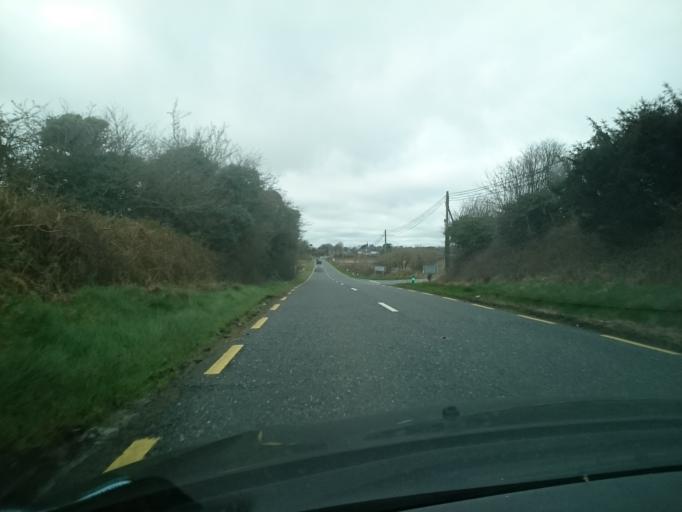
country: IE
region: Connaught
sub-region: Maigh Eo
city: Kiltamagh
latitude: 53.8009
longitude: -9.1131
